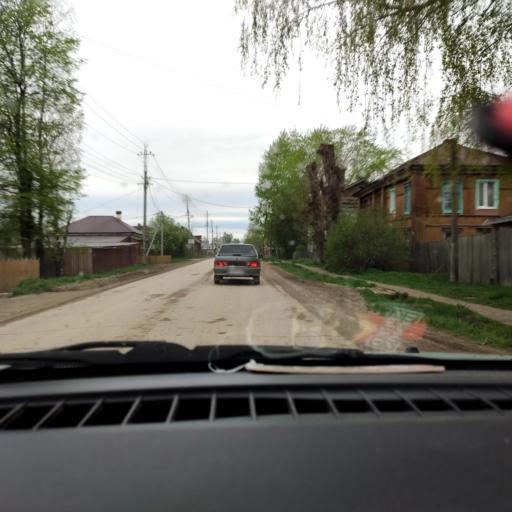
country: RU
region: Perm
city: Kudymkar
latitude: 59.0072
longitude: 54.6622
